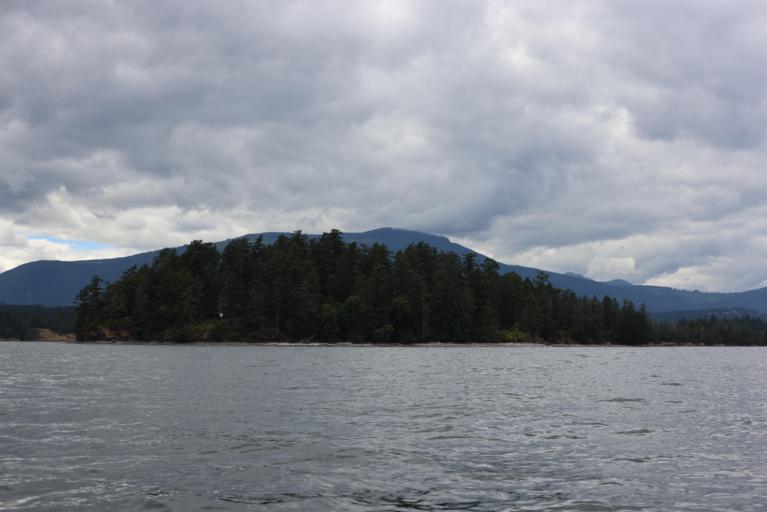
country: CA
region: British Columbia
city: North Cowichan
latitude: 48.9097
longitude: -123.6690
